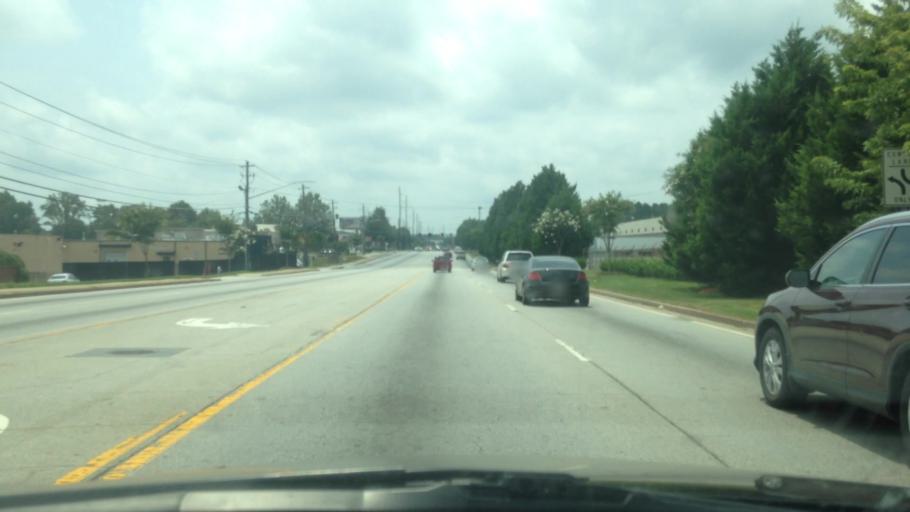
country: US
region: Georgia
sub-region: DeKalb County
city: Tucker
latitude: 33.8447
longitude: -84.2010
